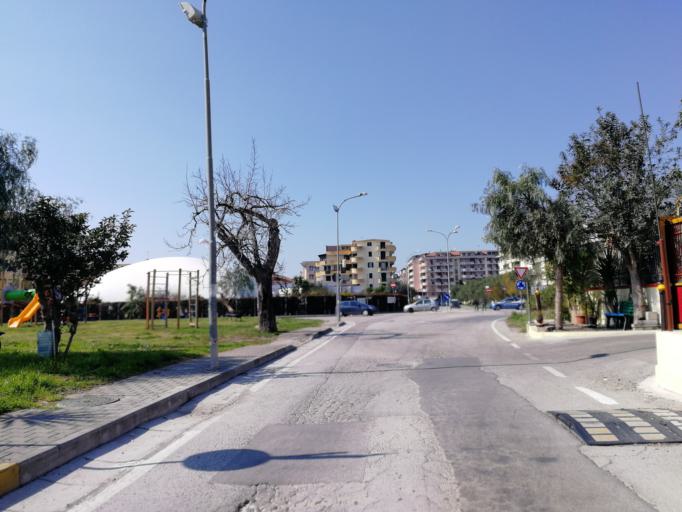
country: IT
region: Campania
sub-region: Provincia di Caserta
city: San Prisco
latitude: 41.0898
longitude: 14.2684
